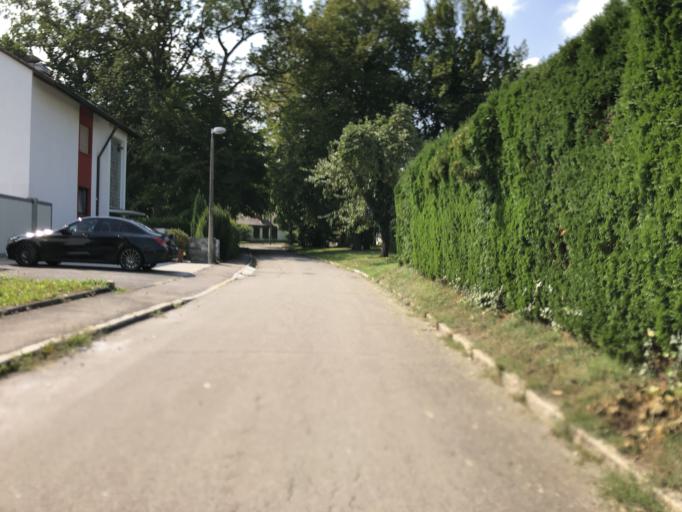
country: DE
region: Baden-Wuerttemberg
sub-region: Regierungsbezirk Stuttgart
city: Sindelfingen
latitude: 48.7229
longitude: 9.0063
